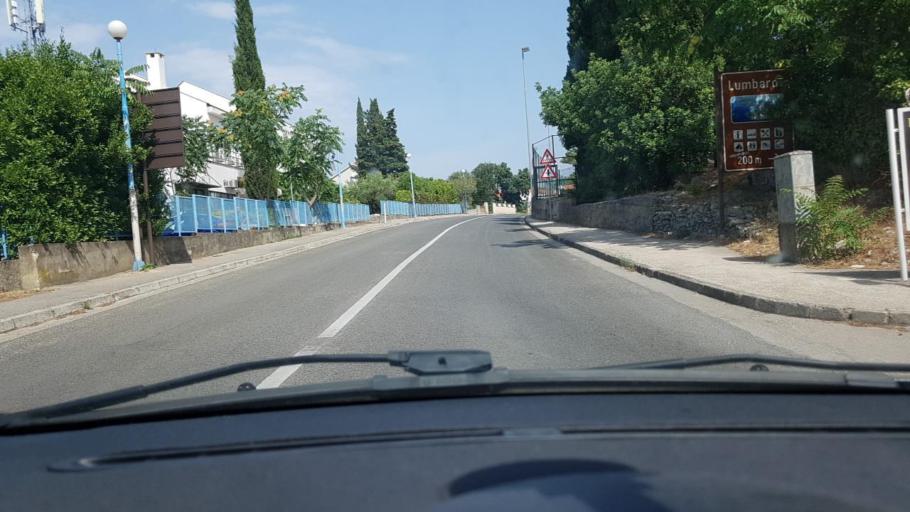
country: HR
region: Dubrovacko-Neretvanska
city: Korcula
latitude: 42.9485
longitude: 17.1363
